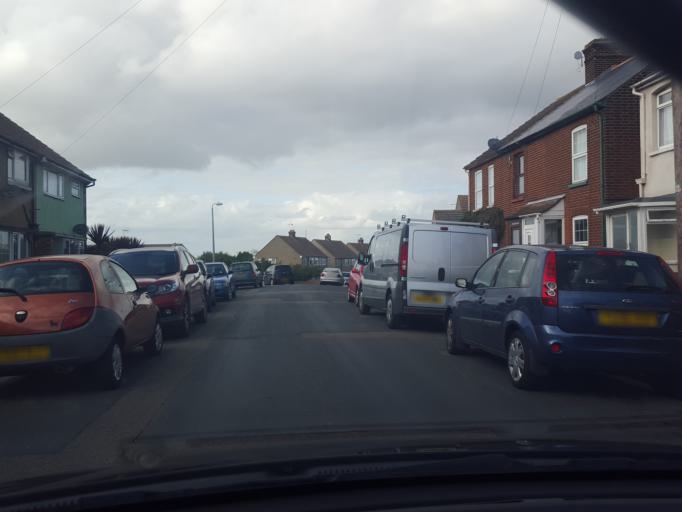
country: GB
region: England
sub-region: Essex
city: Dovercourt
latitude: 51.9345
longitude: 1.2560
